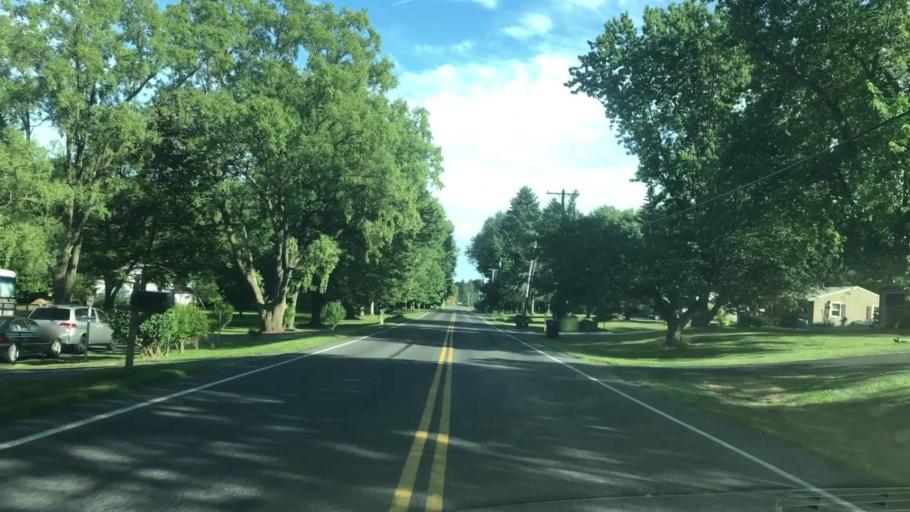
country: US
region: New York
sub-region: Wayne County
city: Macedon
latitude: 43.1188
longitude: -77.3053
